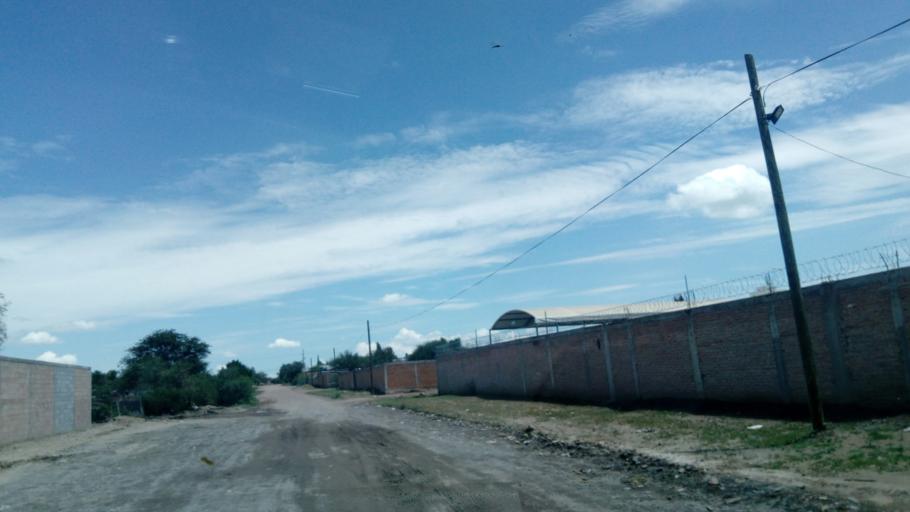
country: MX
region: Durango
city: Victoria de Durango
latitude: 24.0147
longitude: -104.5908
